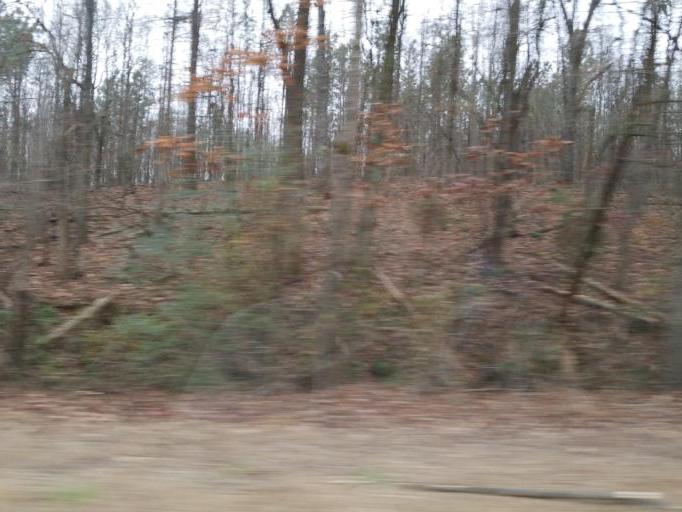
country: US
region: Georgia
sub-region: Dawson County
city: Dawsonville
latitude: 34.4754
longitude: -84.1560
